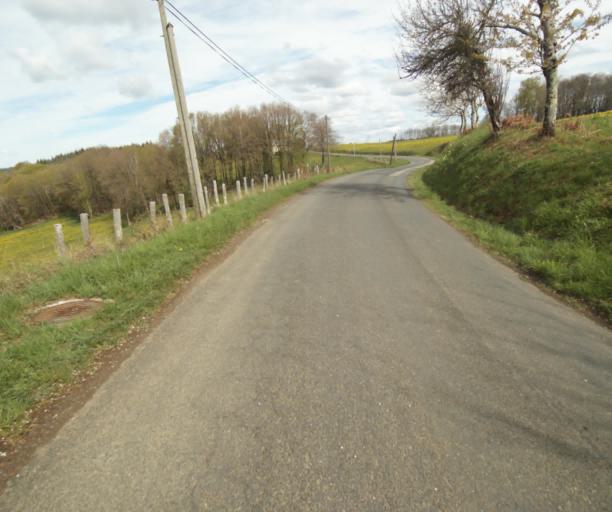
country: FR
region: Limousin
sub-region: Departement de la Correze
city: Laguenne
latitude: 45.2375
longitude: 1.8366
